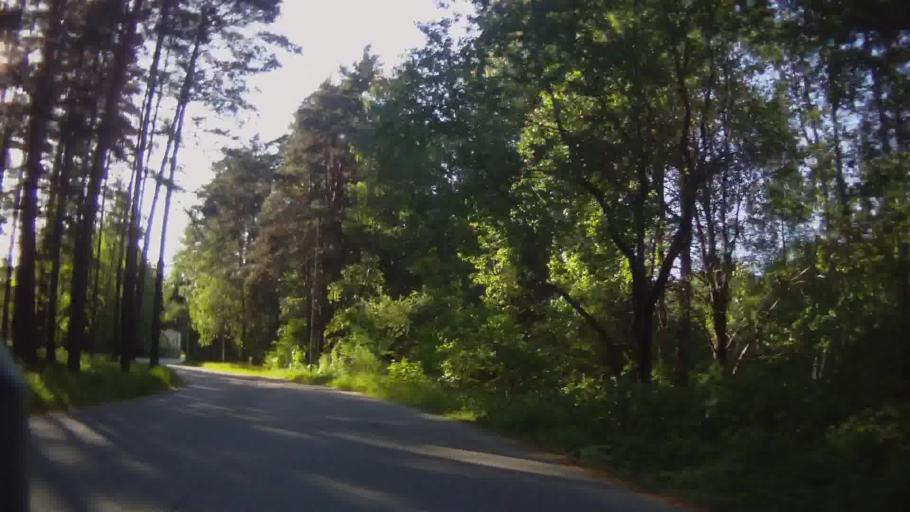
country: LV
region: Riga
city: Bergi
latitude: 56.9788
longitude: 24.3076
